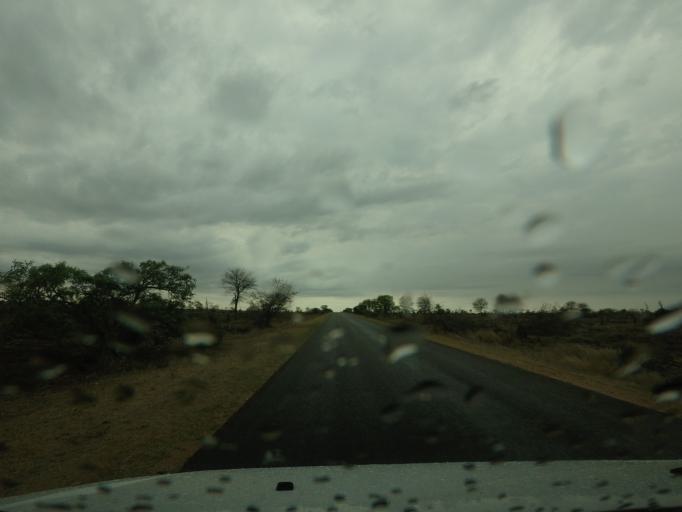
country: ZA
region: Limpopo
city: Thulamahashi
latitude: -24.4753
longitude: 31.3987
